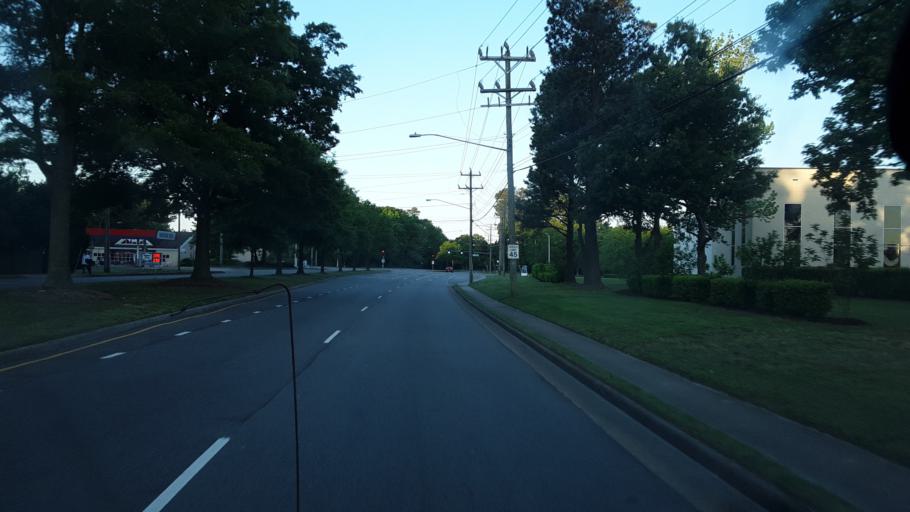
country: US
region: Virginia
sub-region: City of Virginia Beach
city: Virginia Beach
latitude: 36.7766
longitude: -76.0049
